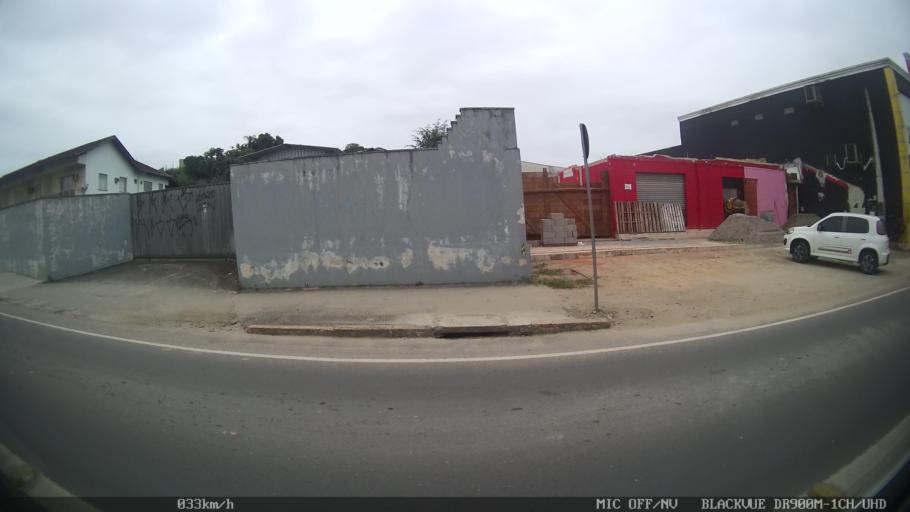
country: BR
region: Santa Catarina
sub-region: Joinville
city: Joinville
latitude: -26.3321
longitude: -48.8470
